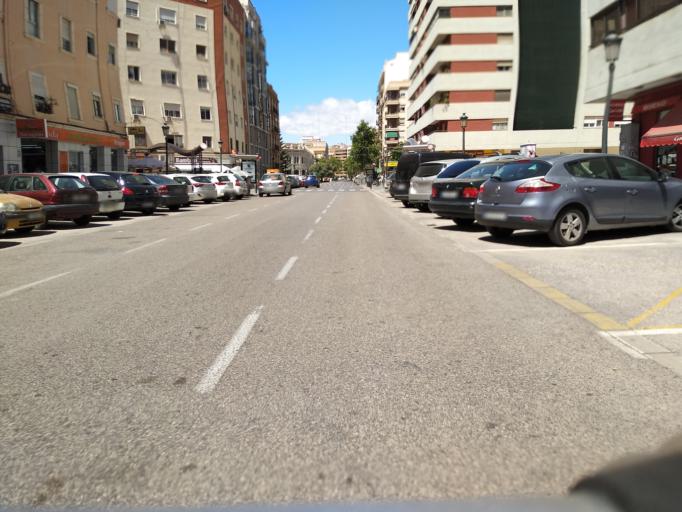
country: ES
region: Valencia
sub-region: Provincia de Valencia
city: Valencia
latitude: 39.4728
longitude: -0.3586
